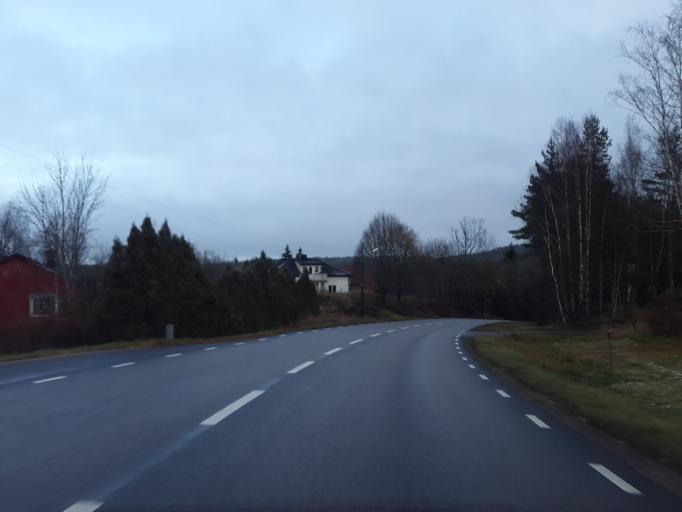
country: SE
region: Vaestra Goetaland
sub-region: Boras Kommun
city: Sandared
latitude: 57.8089
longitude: 12.7520
